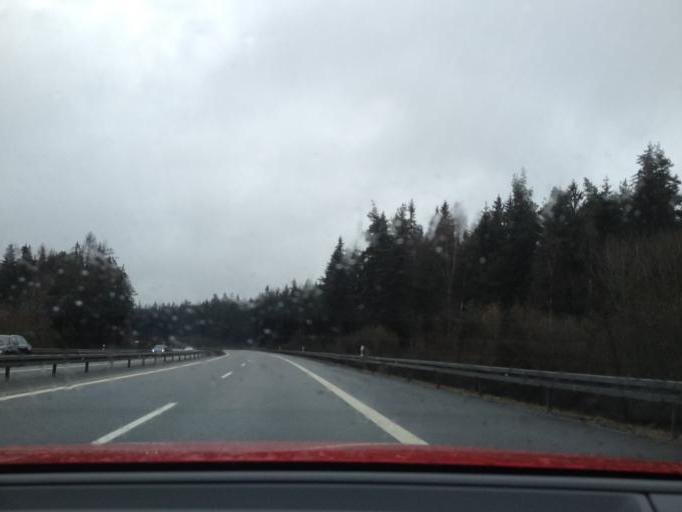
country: DE
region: Bavaria
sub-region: Upper Franconia
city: Rehau
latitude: 50.2333
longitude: 12.0652
